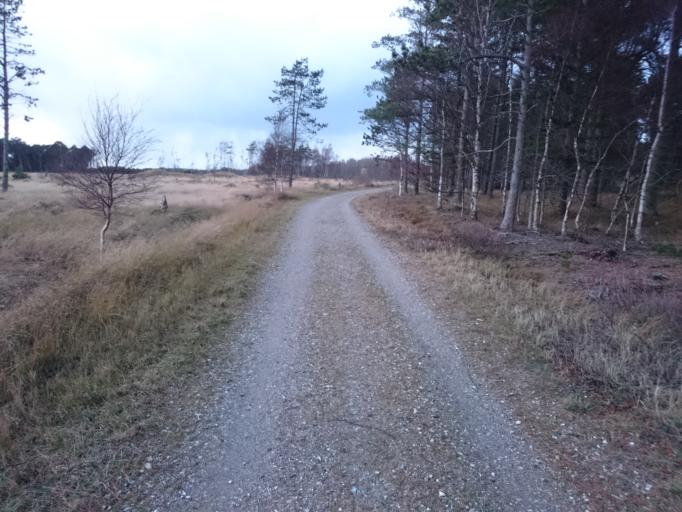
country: DK
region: North Denmark
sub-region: Frederikshavn Kommune
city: Skagen
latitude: 57.7121
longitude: 10.5455
